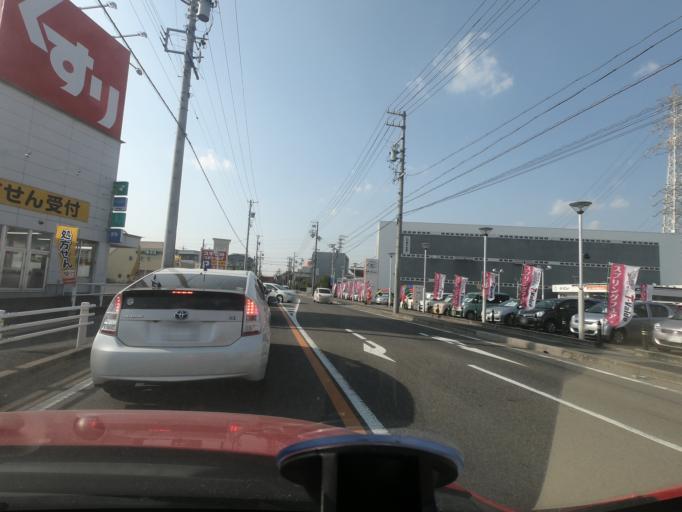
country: JP
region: Aichi
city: Kasugai
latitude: 35.2619
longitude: 136.9941
